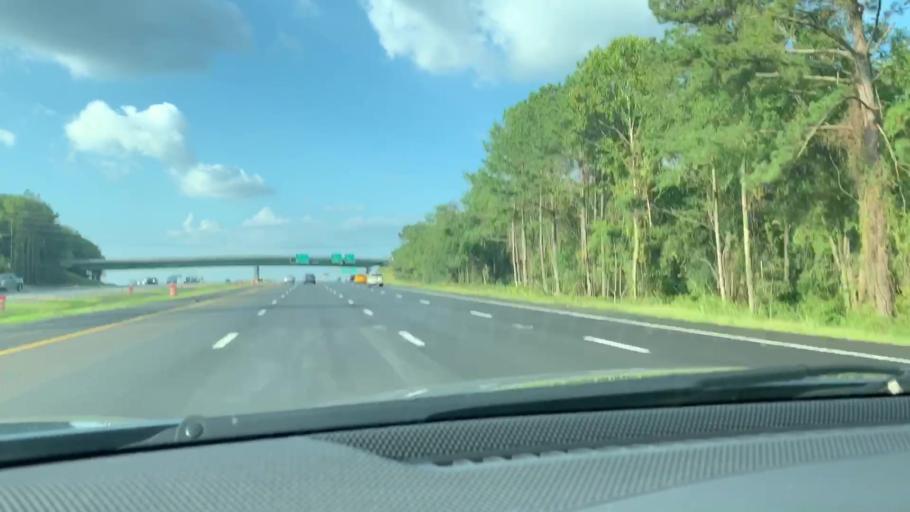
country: US
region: South Carolina
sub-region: Richland County
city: Woodfield
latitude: 34.0614
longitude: -80.9220
